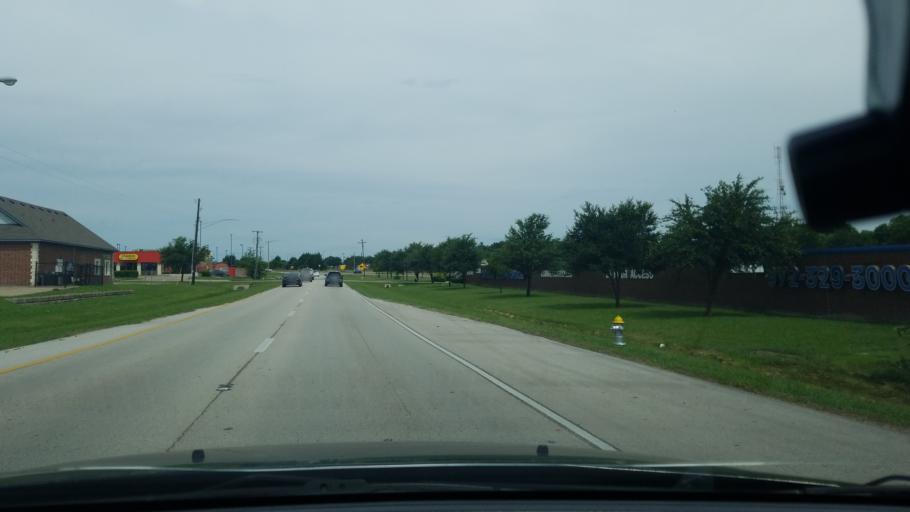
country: US
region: Texas
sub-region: Dallas County
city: Mesquite
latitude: 32.7648
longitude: -96.5836
